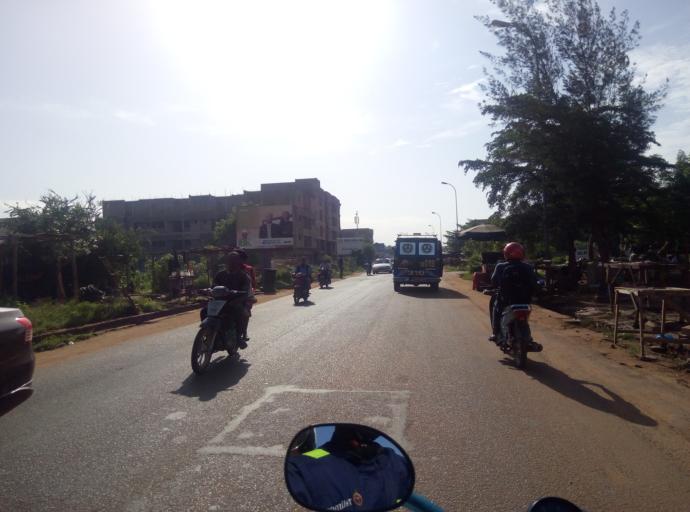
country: ML
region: Bamako
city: Bamako
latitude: 12.6535
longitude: -7.9354
